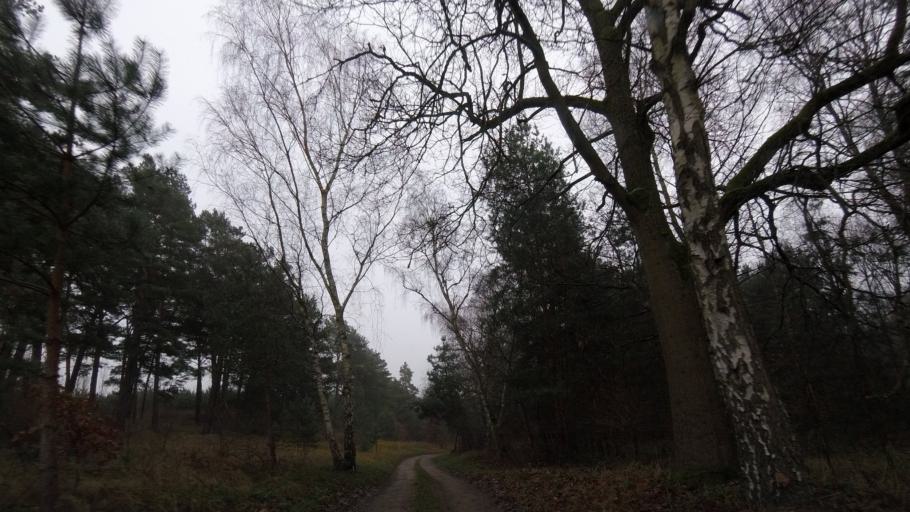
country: DE
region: Brandenburg
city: Treuenbrietzen
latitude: 52.0620
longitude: 12.8829
